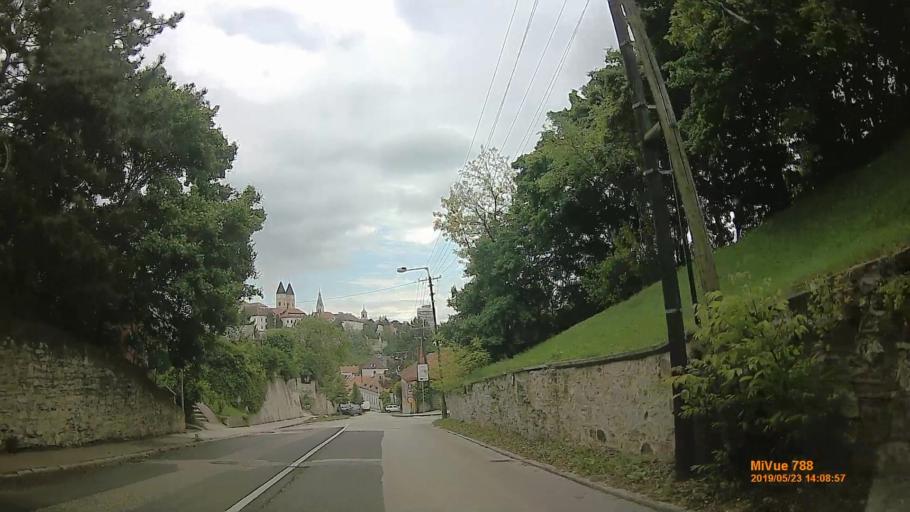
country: HU
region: Veszprem
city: Veszprem
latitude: 47.0984
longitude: 17.8969
